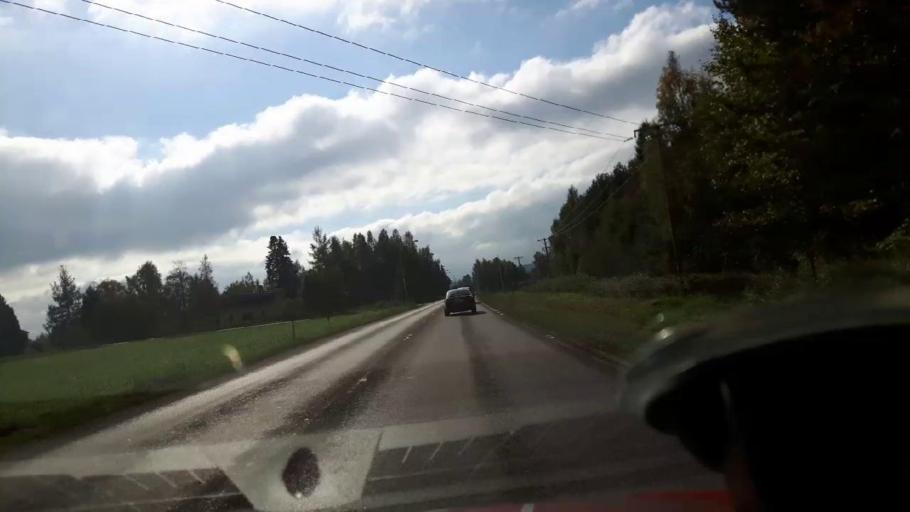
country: SE
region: Gaevleborg
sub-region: Bollnas Kommun
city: Arbra
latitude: 61.5235
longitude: 16.3640
